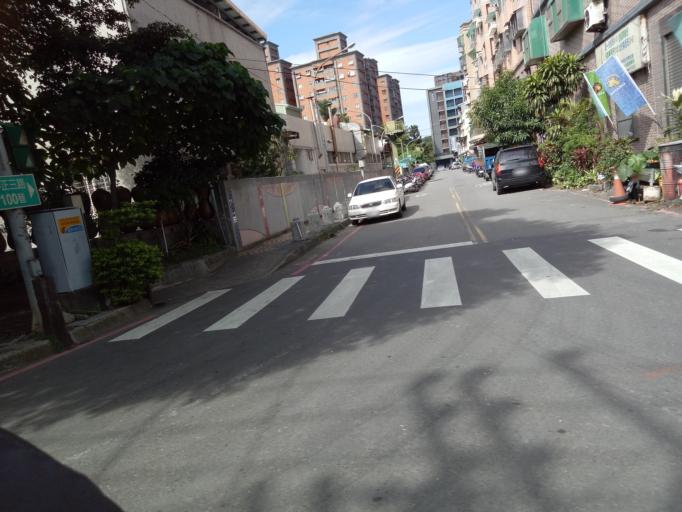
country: TW
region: Taiwan
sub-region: Taoyuan
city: Taoyuan
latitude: 24.9410
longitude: 121.3382
